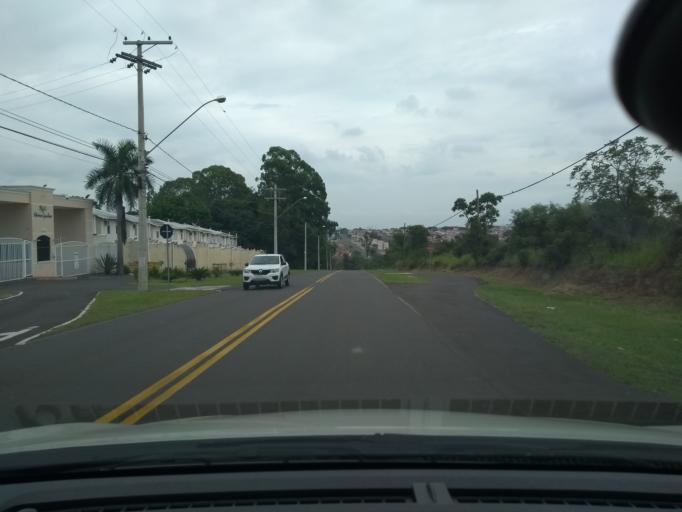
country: BR
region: Sao Paulo
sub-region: Rio Claro
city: Rio Claro
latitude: -22.3671
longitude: -47.5317
